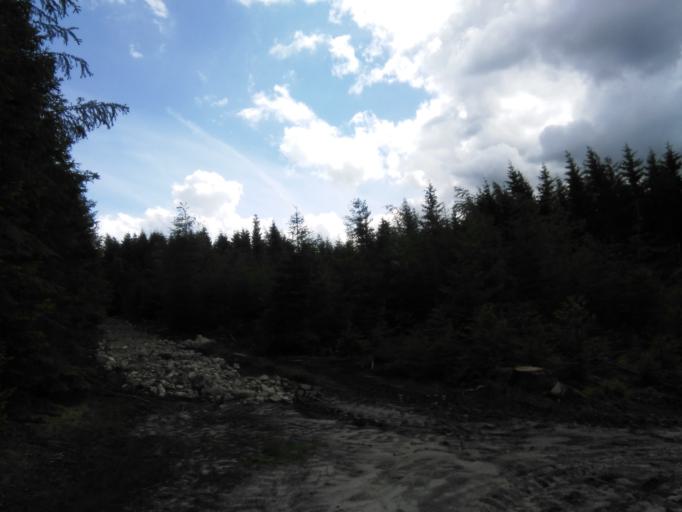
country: DK
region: Central Jutland
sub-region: Silkeborg Kommune
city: Virklund
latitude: 56.0687
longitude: 9.4623
